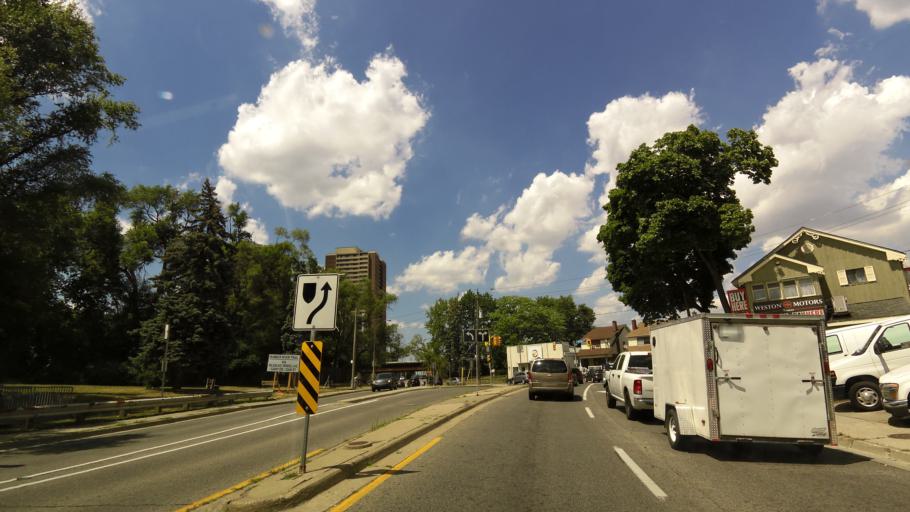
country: CA
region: Ontario
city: Etobicoke
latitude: 43.7059
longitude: -79.5323
